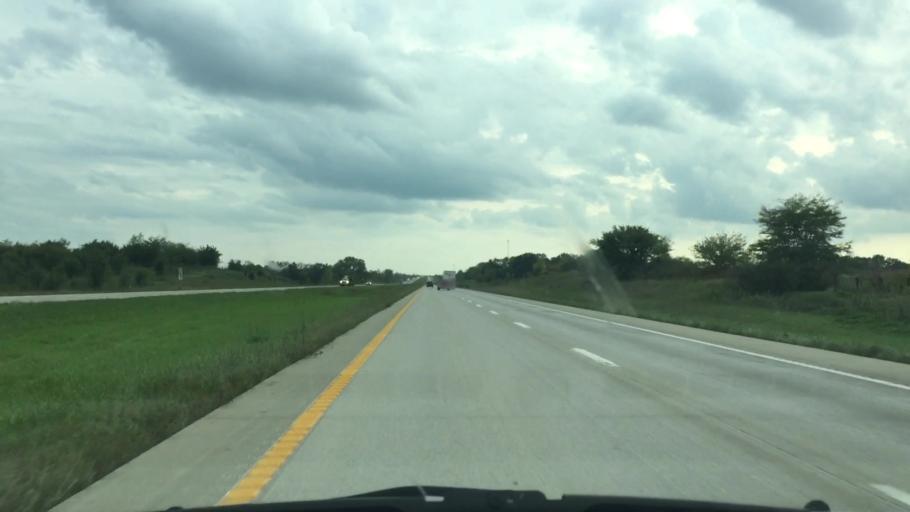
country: US
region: Missouri
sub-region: Clinton County
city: Lathrop
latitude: 39.6117
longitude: -94.2505
